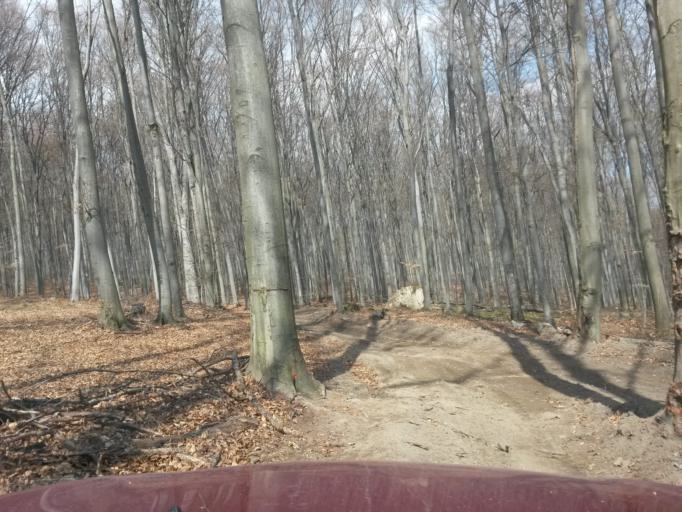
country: SK
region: Presovsky
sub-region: Okres Presov
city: Presov
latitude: 48.9312
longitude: 21.1405
